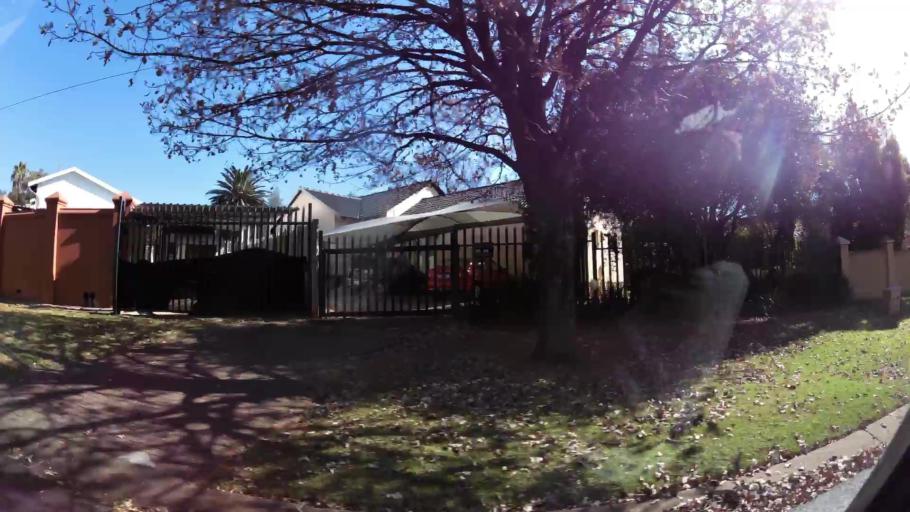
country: ZA
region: Gauteng
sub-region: City of Johannesburg Metropolitan Municipality
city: Roodepoort
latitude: -26.1178
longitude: 27.8687
